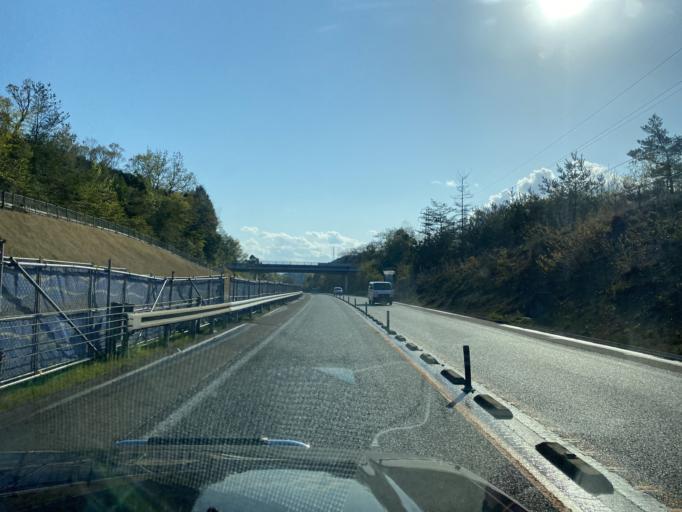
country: JP
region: Kyoto
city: Ayabe
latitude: 35.3274
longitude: 135.2247
